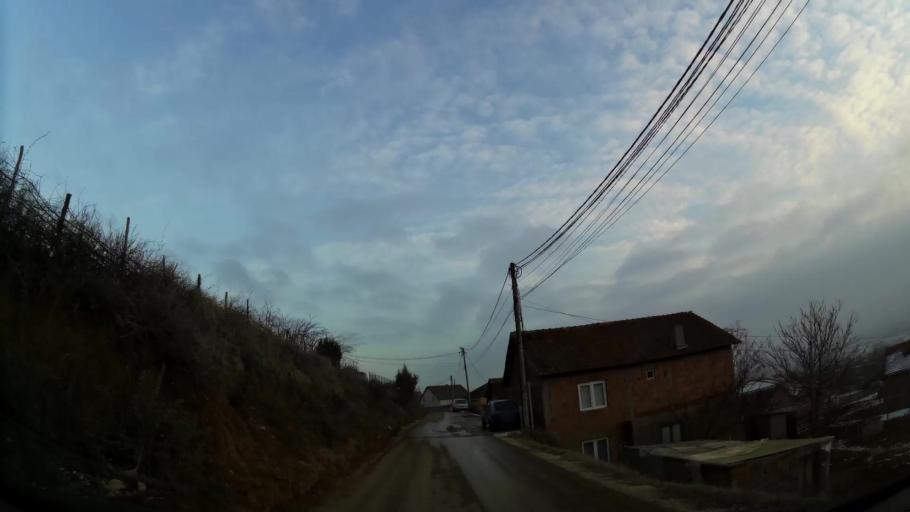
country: MK
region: Aracinovo
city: Arachinovo
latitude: 42.0318
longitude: 21.5560
